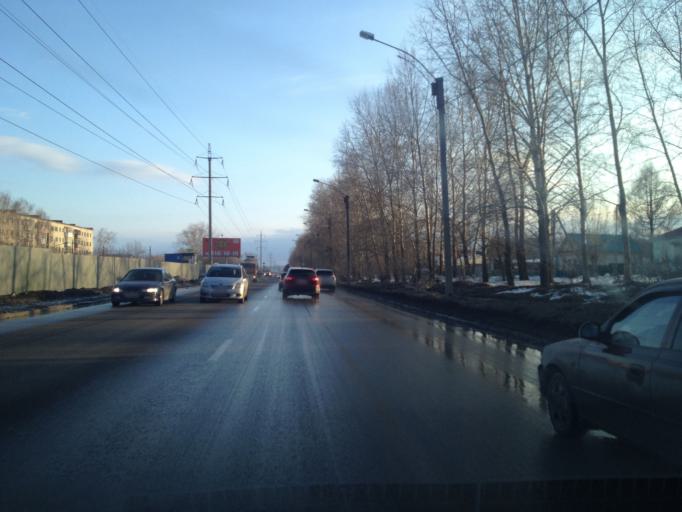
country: RU
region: Sverdlovsk
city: Sovkhoznyy
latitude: 56.7713
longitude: 60.5966
